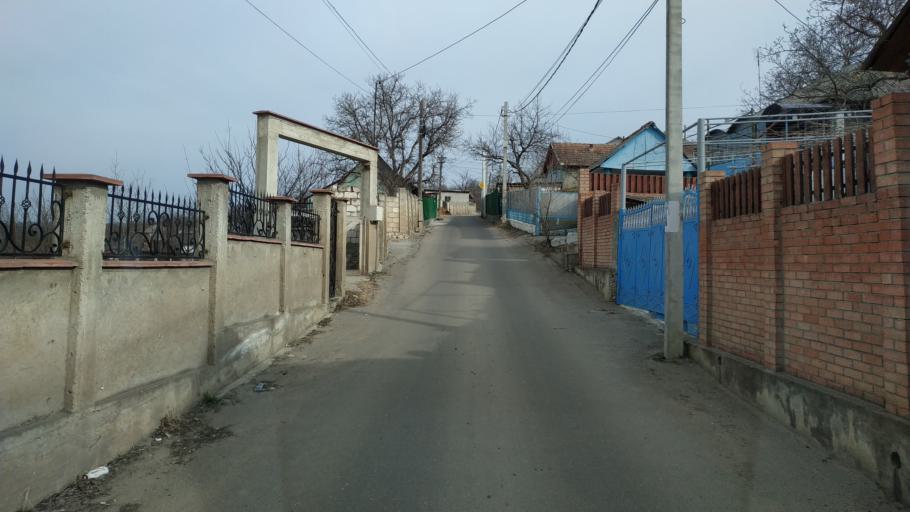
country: MD
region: Chisinau
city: Vatra
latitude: 47.0878
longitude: 28.7740
